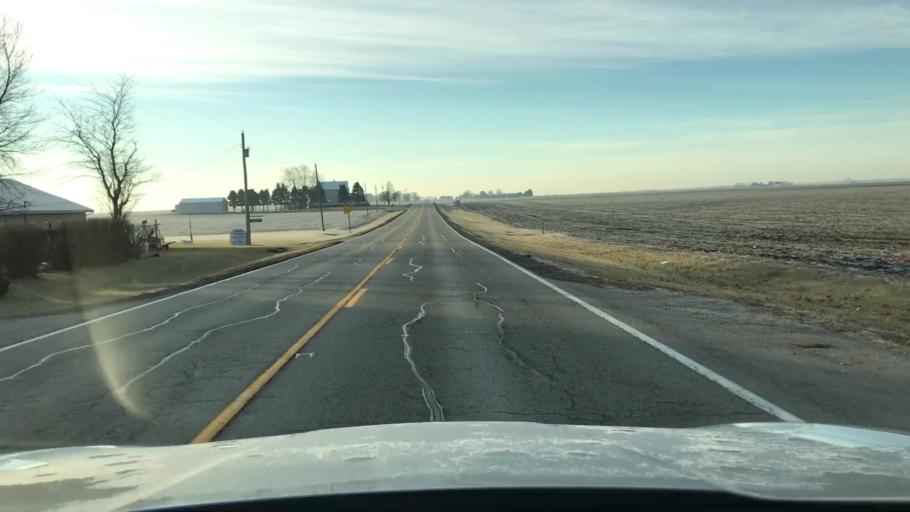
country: US
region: Illinois
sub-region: McLean County
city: Hudson
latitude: 40.6030
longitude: -88.9451
